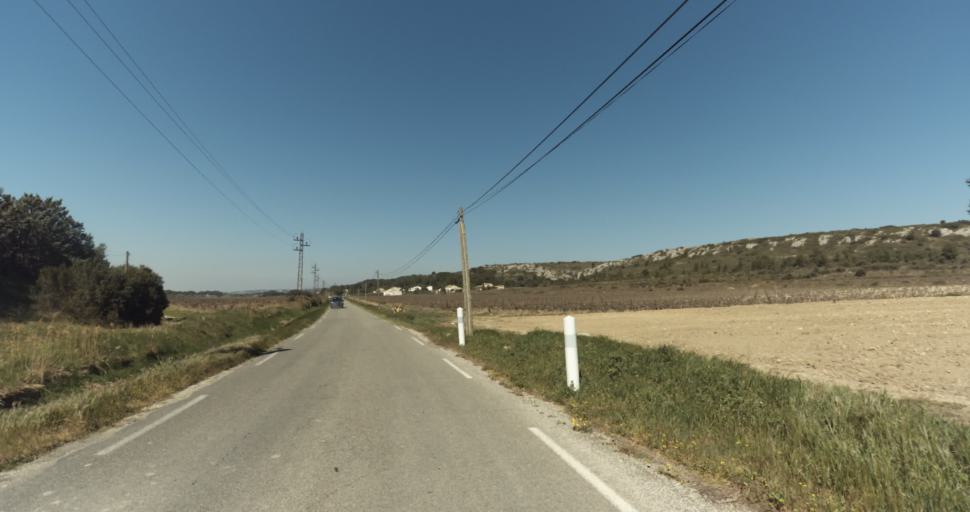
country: FR
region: Provence-Alpes-Cote d'Azur
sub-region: Departement des Bouches-du-Rhone
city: Pelissanne
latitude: 43.6049
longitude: 5.1889
